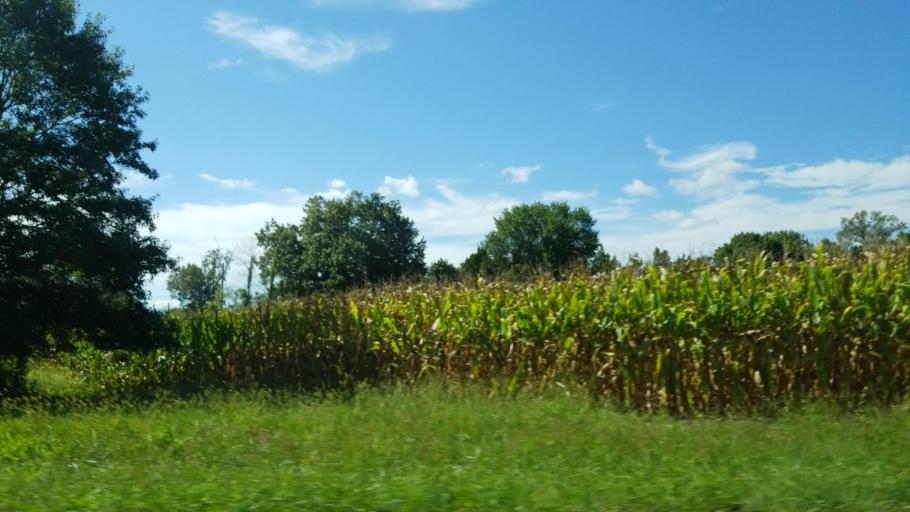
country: US
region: Illinois
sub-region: Williamson County
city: Marion
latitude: 37.7565
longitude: -88.8729
